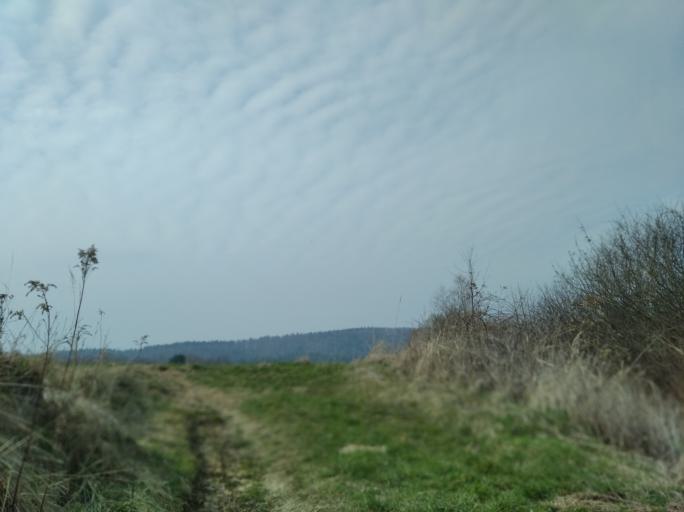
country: PL
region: Subcarpathian Voivodeship
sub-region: Powiat strzyzowski
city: Strzyzow
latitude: 49.8179
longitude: 21.8327
